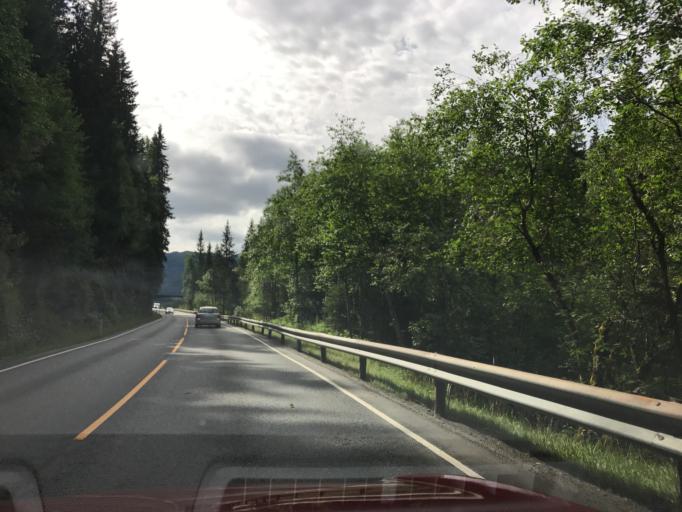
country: NO
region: Hordaland
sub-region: Voss
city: Voss
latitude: 60.6188
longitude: 6.5340
